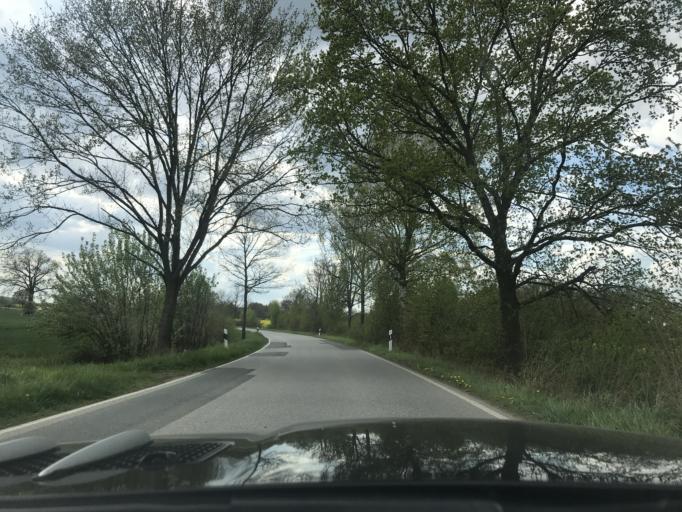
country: DE
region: Schleswig-Holstein
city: Timmendorfer Strand
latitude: 53.9586
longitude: 10.7926
